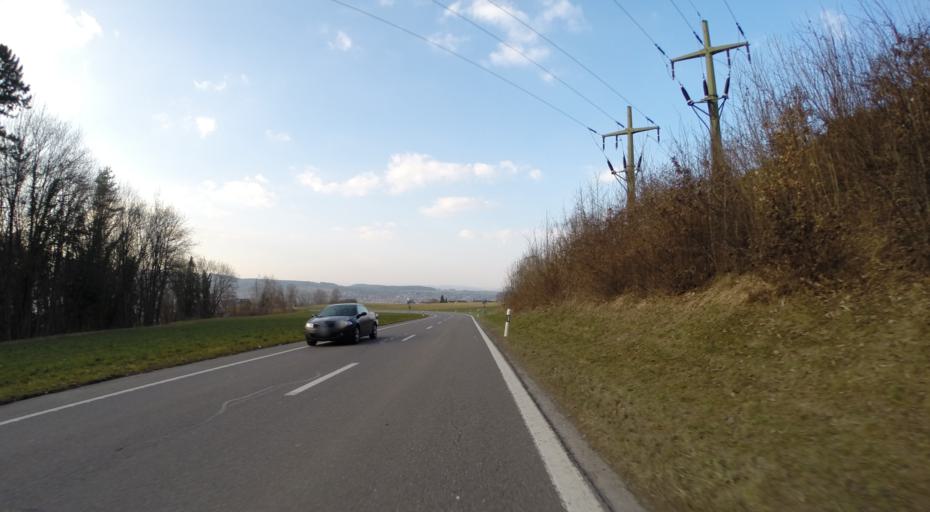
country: CH
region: Thurgau
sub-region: Frauenfeld District
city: Steckborn
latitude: 47.6573
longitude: 8.9898
